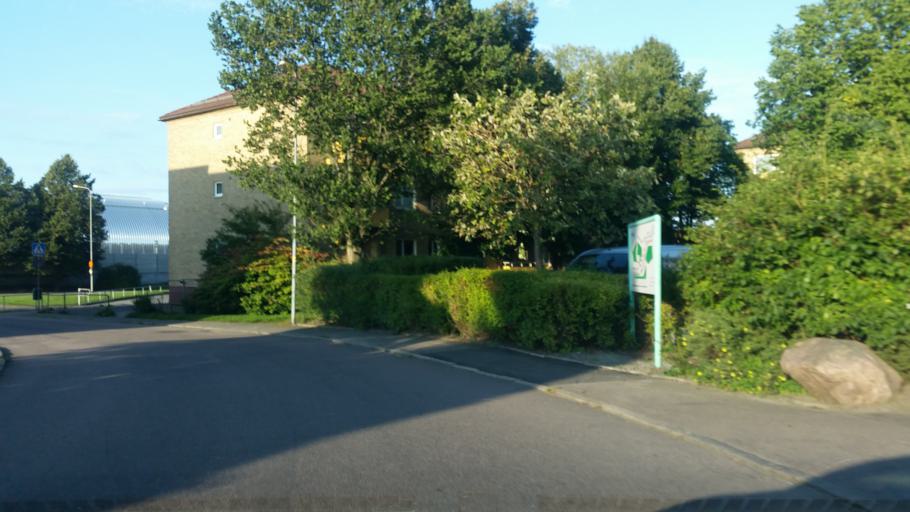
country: SE
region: Vaestra Goetaland
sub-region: Partille Kommun
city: Partille
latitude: 57.7382
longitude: 12.1169
